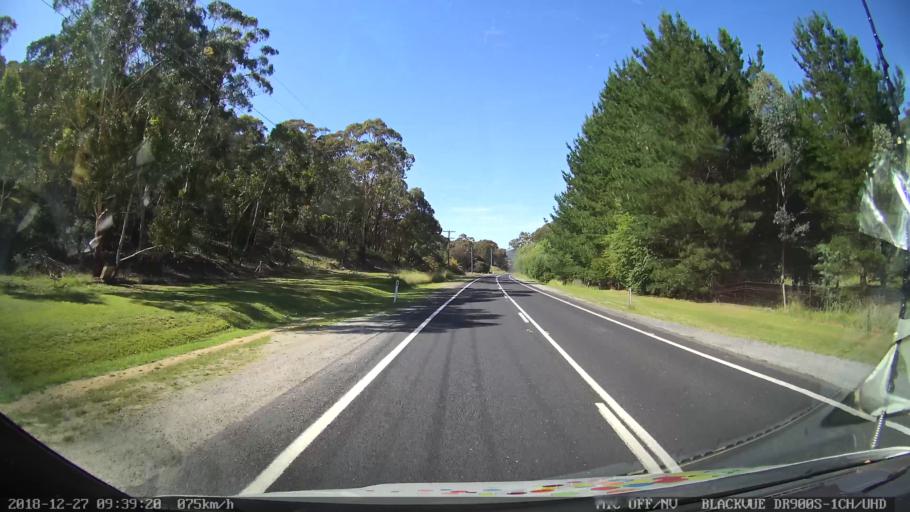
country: AU
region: New South Wales
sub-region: Lithgow
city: Portland
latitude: -33.2917
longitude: 150.0353
